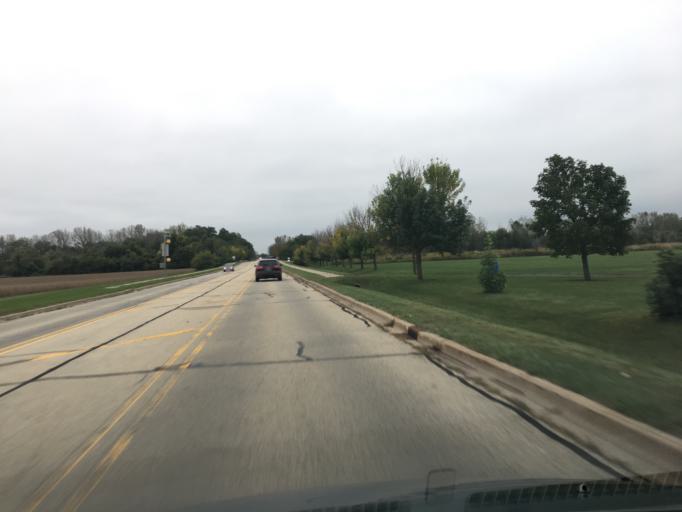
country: US
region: Illinois
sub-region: Will County
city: Plainfield
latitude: 41.6485
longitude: -88.1648
